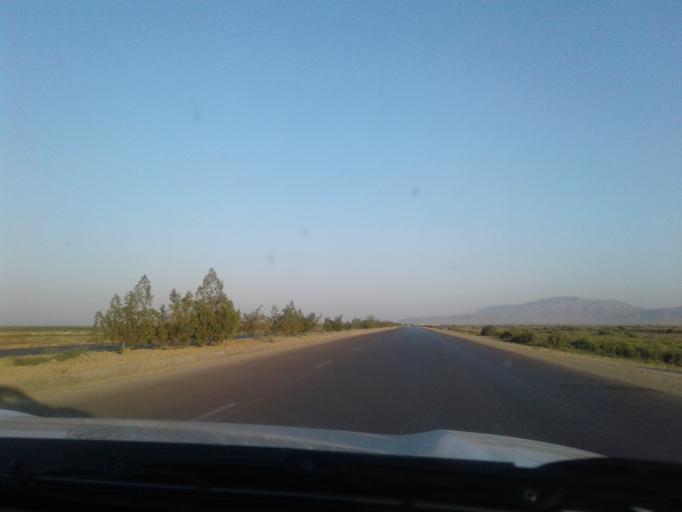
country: TM
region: Ahal
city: Baharly
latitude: 38.3642
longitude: 57.5268
